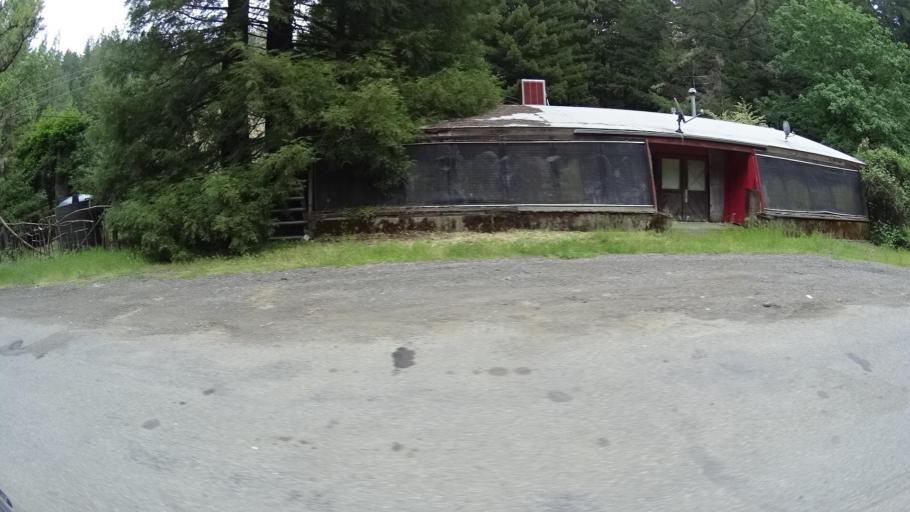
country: US
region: California
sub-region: Humboldt County
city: Redway
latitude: 40.1268
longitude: -123.8459
